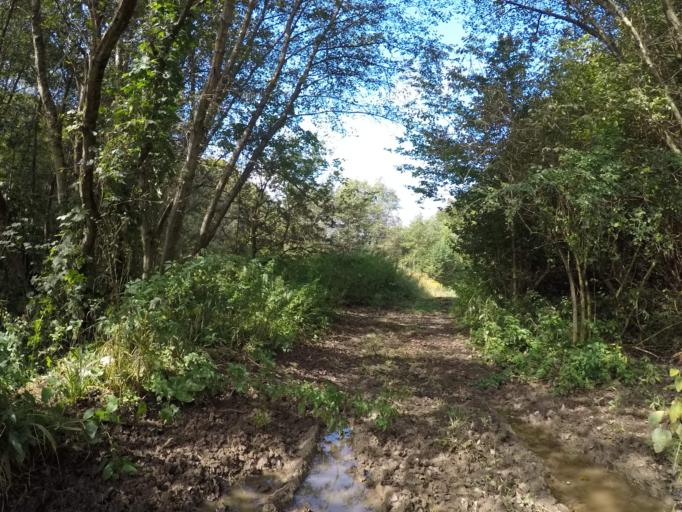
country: SK
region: Presovsky
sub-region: Okres Presov
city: Presov
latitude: 48.9331
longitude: 21.1641
